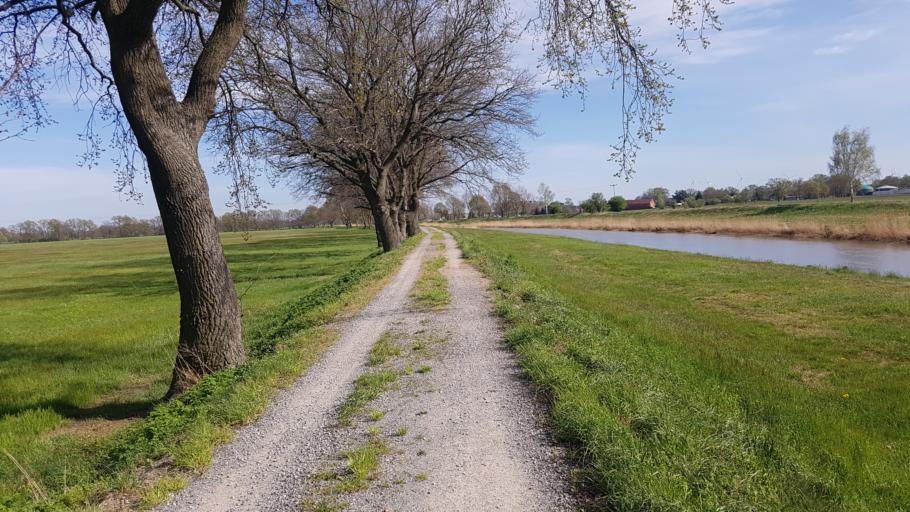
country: DE
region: Brandenburg
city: Falkenberg
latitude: 51.6205
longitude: 13.2890
